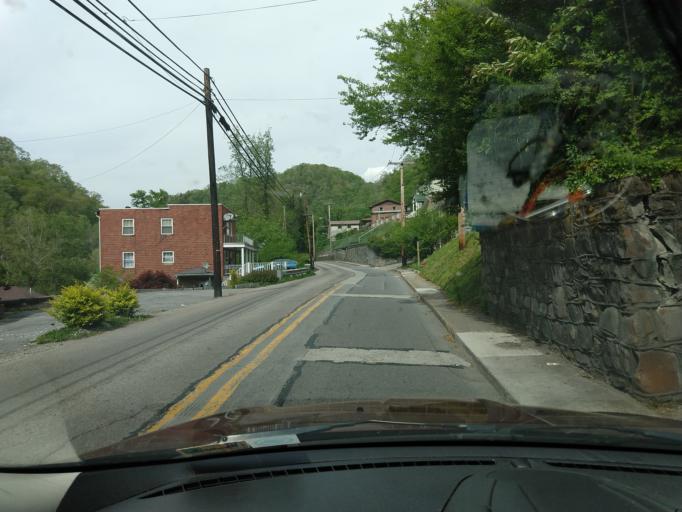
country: US
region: West Virginia
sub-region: McDowell County
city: Welch
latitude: 37.4218
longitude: -81.5872
